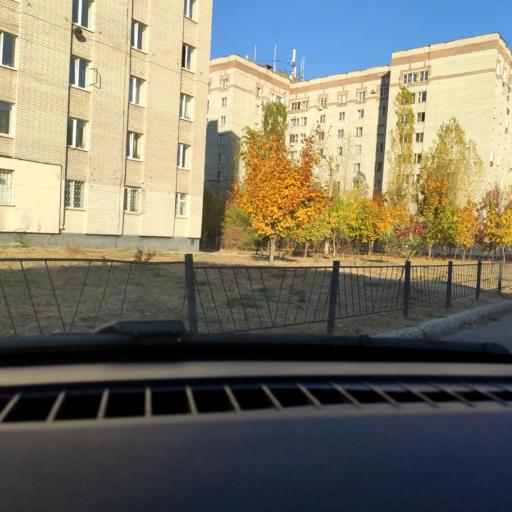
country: RU
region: Voronezj
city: Podgornoye
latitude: 51.7281
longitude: 39.2015
